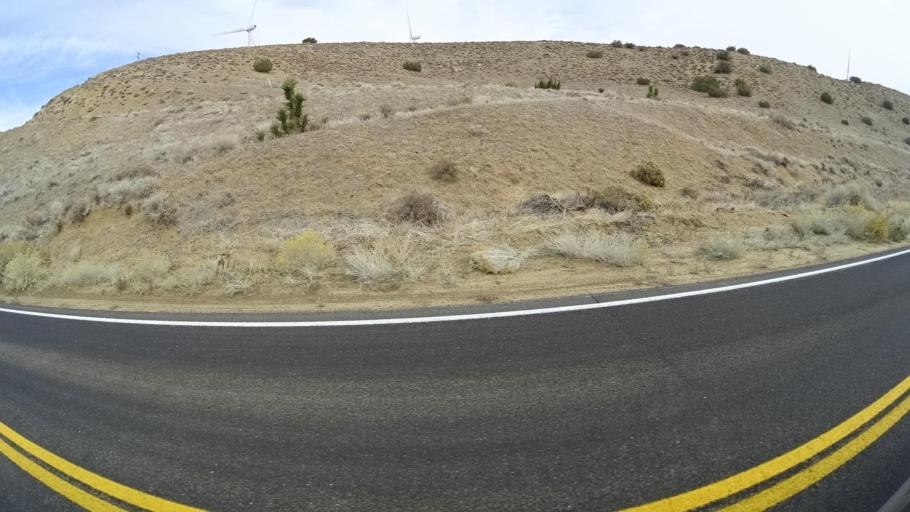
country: US
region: California
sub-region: Kern County
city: Tehachapi
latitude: 35.0508
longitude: -118.3285
